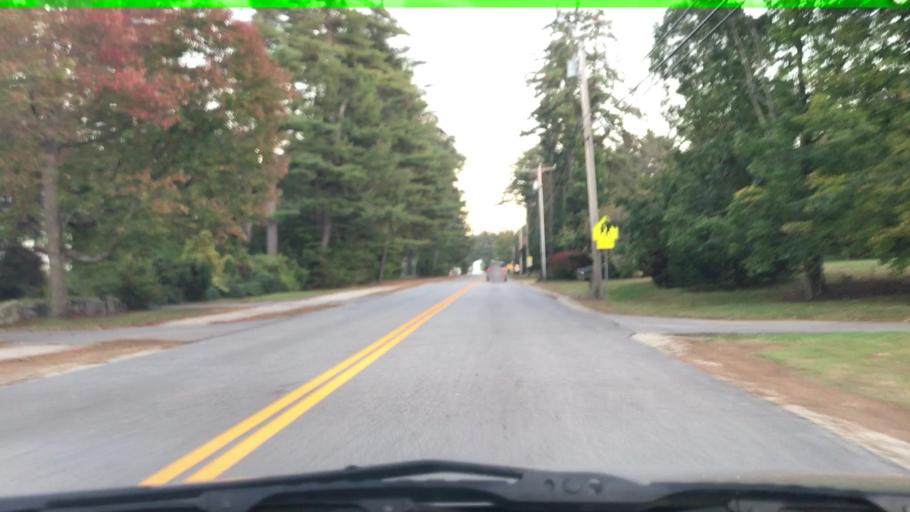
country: US
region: New Hampshire
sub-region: Cheshire County
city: Swanzey
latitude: 42.8768
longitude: -72.2847
